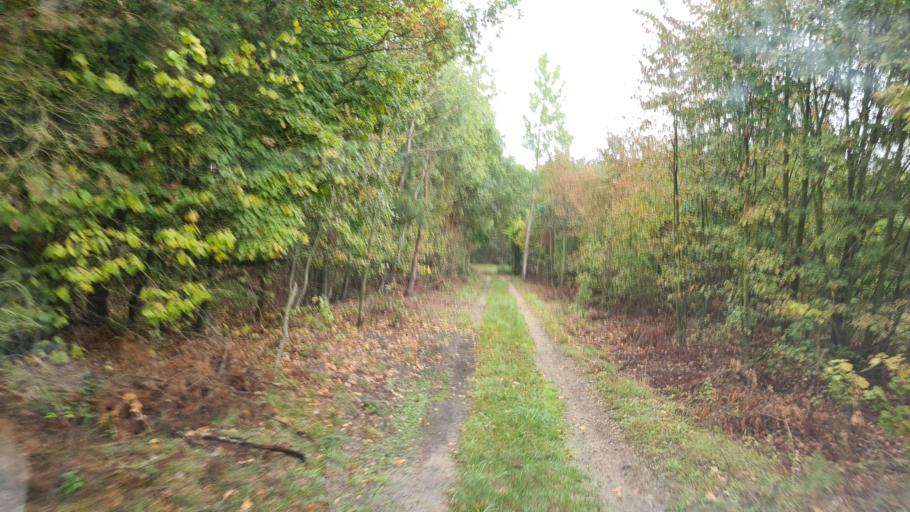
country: DE
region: Brandenburg
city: Altdobern
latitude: 51.6724
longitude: 14.1081
